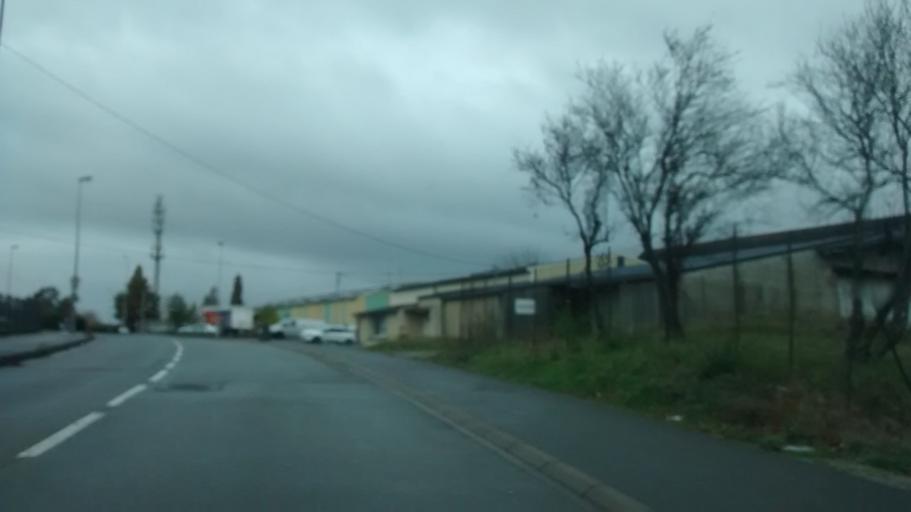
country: FR
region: Brittany
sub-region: Departement d'Ille-et-Vilaine
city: Noyal-sur-Vilaine
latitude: 48.1059
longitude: -1.5191
